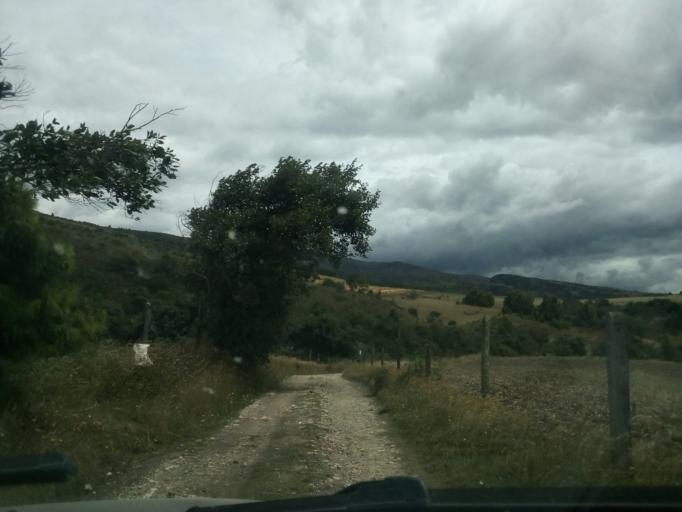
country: CO
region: Boyaca
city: Pesca
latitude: 5.6066
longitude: -73.1116
